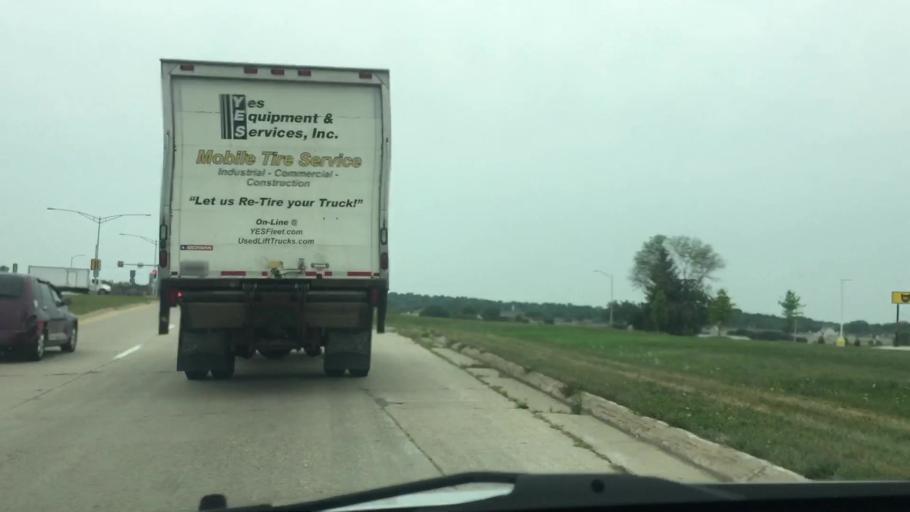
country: US
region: Wisconsin
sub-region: Waukesha County
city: Pewaukee
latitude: 43.0523
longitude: -88.2540
